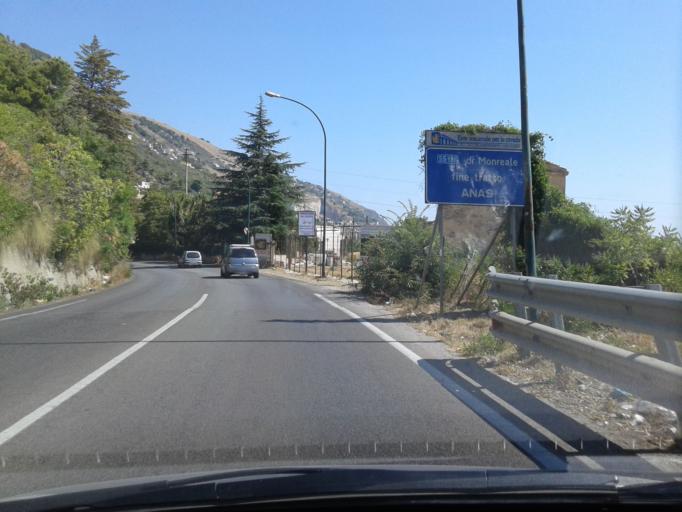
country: IT
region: Sicily
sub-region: Palermo
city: Cannizzaro-Favara
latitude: 38.0720
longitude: 13.2769
